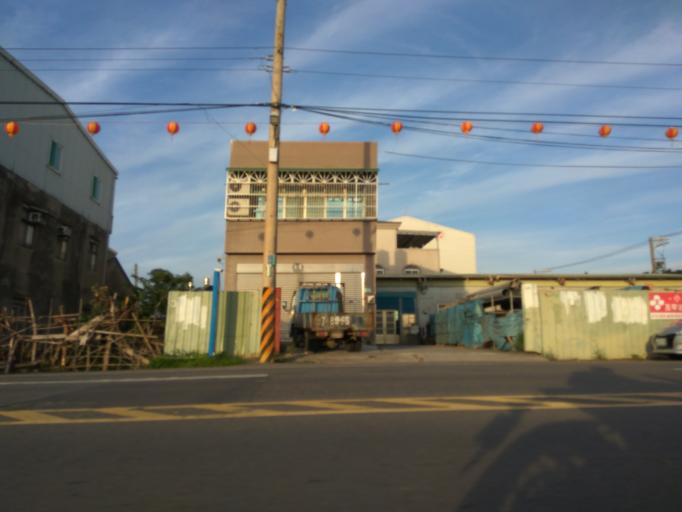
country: TW
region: Taiwan
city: Taoyuan City
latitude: 25.0047
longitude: 121.1499
